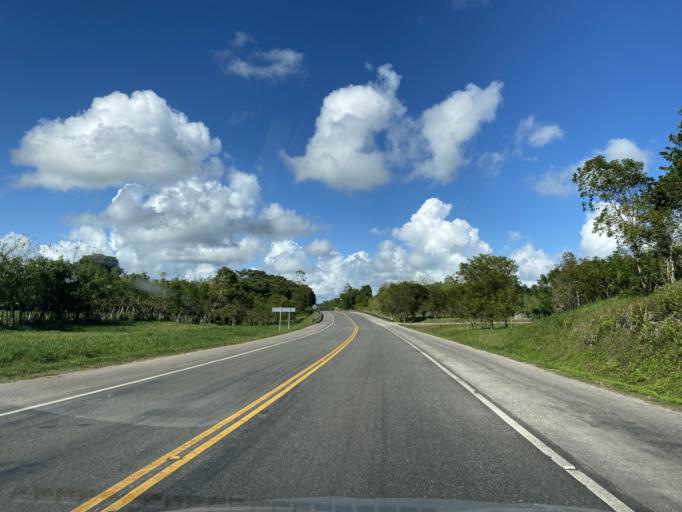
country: DO
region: Monte Plata
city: Majagual
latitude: 19.0246
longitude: -69.8228
